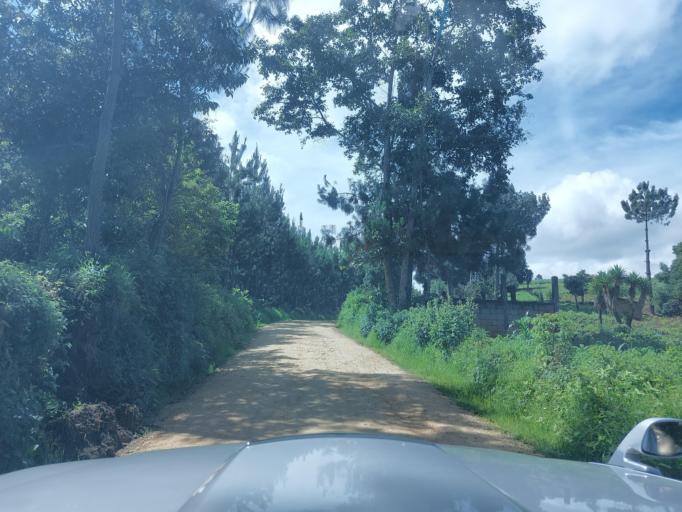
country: GT
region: Chimaltenango
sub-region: Municipio de San Juan Comalapa
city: Comalapa
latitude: 14.7588
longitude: -90.8780
